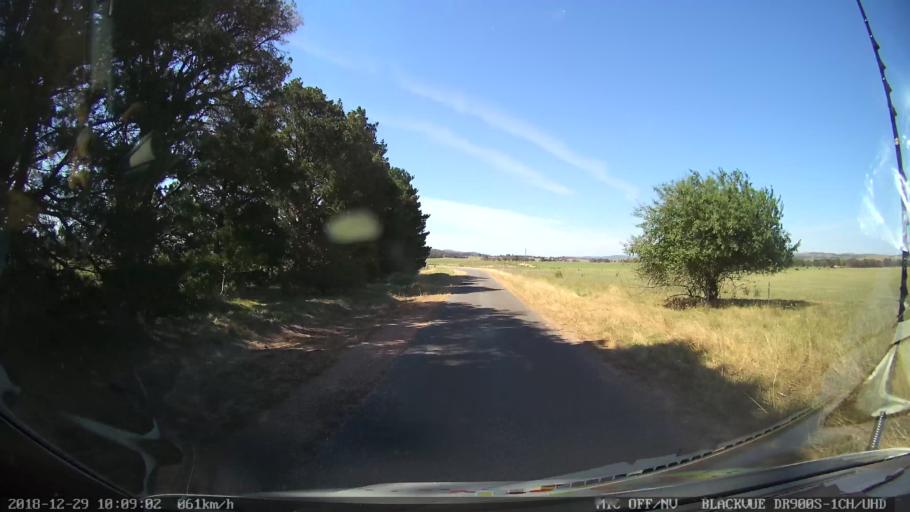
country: AU
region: New South Wales
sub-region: Yass Valley
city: Gundaroo
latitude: -34.8620
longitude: 149.4589
